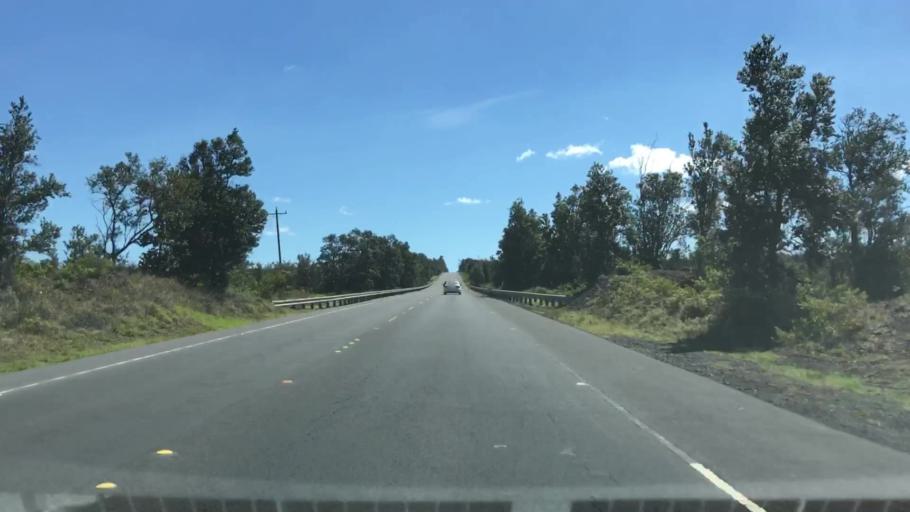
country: US
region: Hawaii
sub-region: Hawaii County
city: Volcano
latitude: 19.4193
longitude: -155.3068
